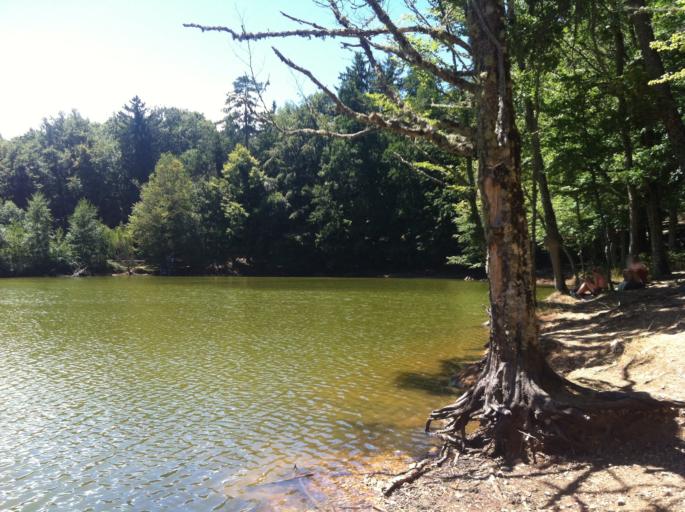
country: IT
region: Apulia
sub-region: Provincia di Foggia
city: Vico del Gargano
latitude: 41.8177
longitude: 15.9966
